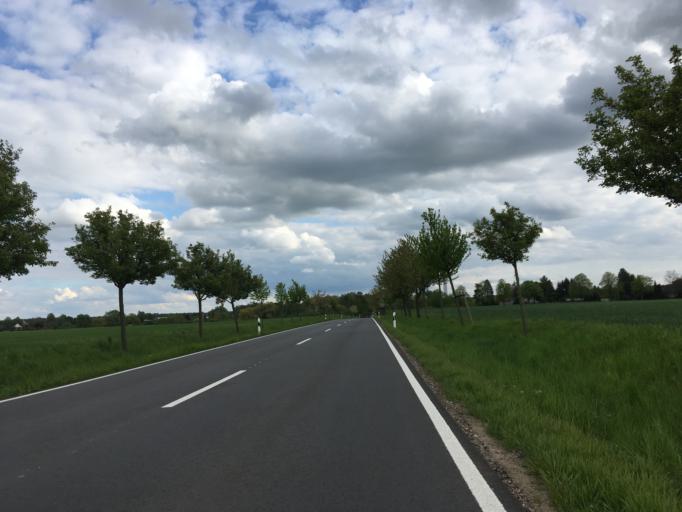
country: DE
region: Brandenburg
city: Bernau bei Berlin
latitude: 52.6493
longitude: 13.6055
